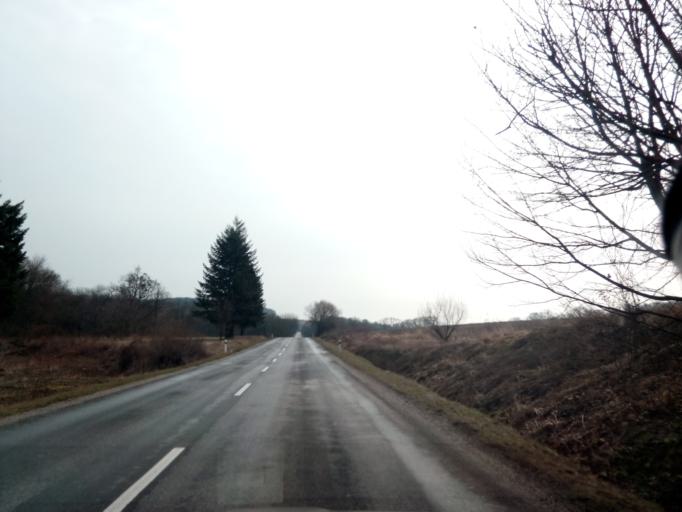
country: SK
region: Kosicky
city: Secovce
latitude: 48.6333
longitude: 21.5116
